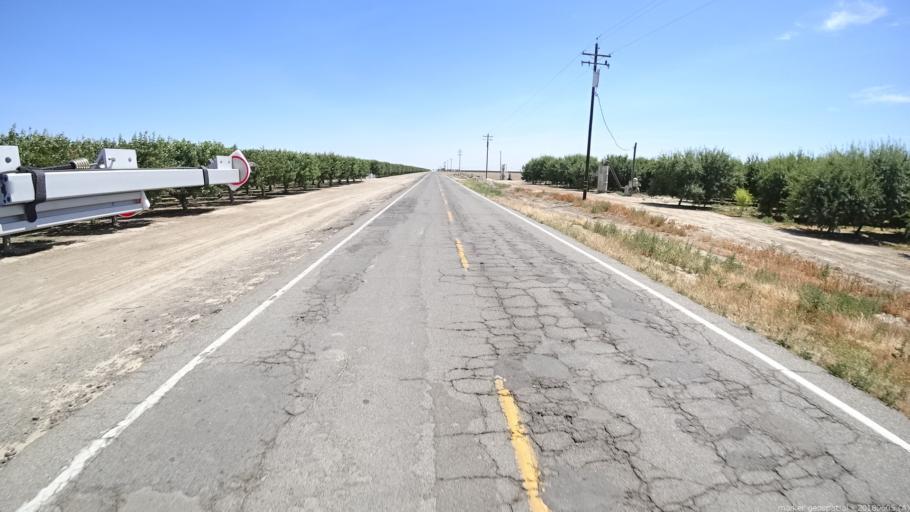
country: US
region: California
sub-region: Fresno County
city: Firebaugh
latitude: 36.9605
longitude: -120.3827
